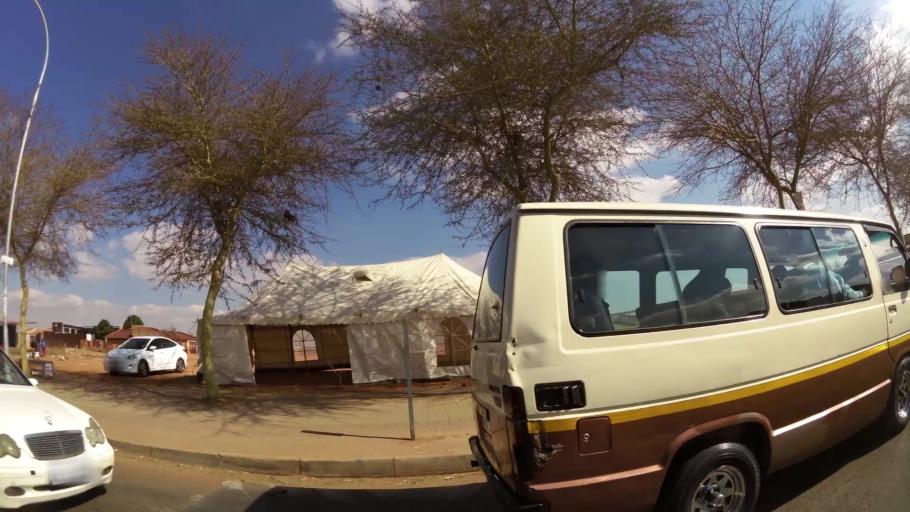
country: ZA
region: Gauteng
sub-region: Ekurhuleni Metropolitan Municipality
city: Tembisa
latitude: -26.0050
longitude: 28.2120
